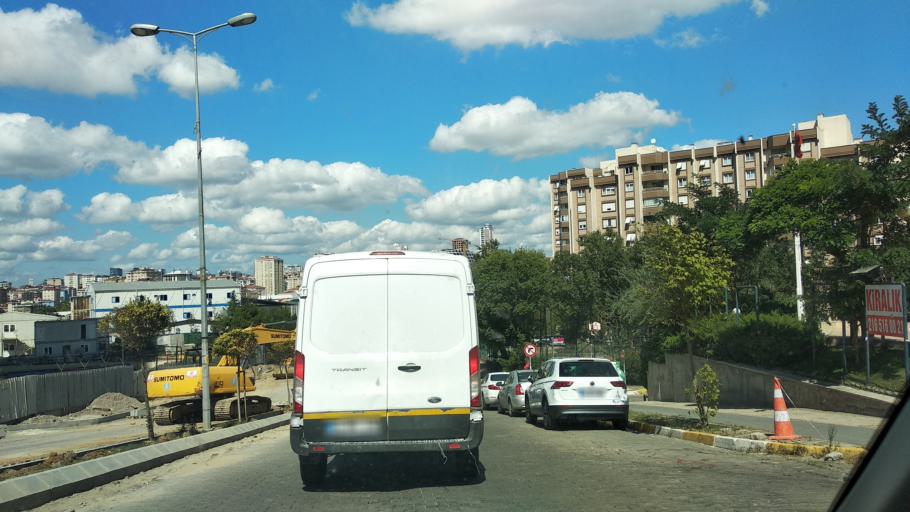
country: TR
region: Istanbul
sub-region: Atasehir
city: Atasehir
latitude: 40.9940
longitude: 29.1279
